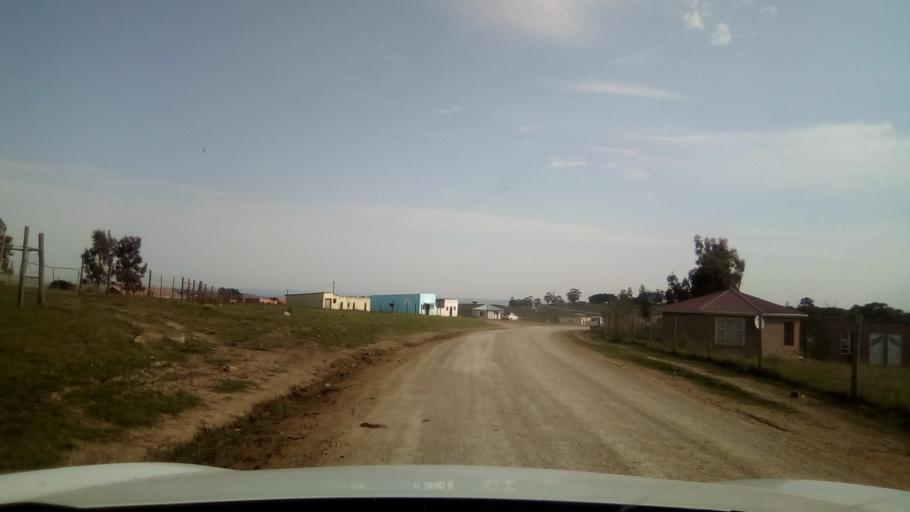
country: ZA
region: Eastern Cape
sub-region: Buffalo City Metropolitan Municipality
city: Bhisho
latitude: -32.9866
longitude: 27.2690
